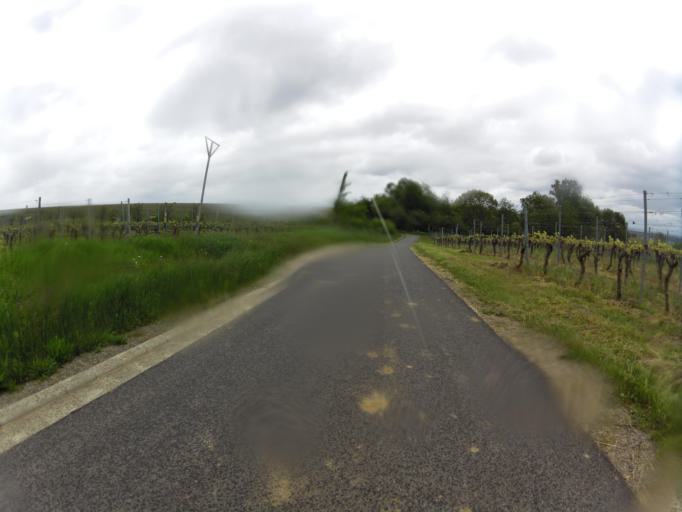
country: DE
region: Bavaria
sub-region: Regierungsbezirk Unterfranken
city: Sommerach
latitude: 49.8437
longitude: 10.2060
